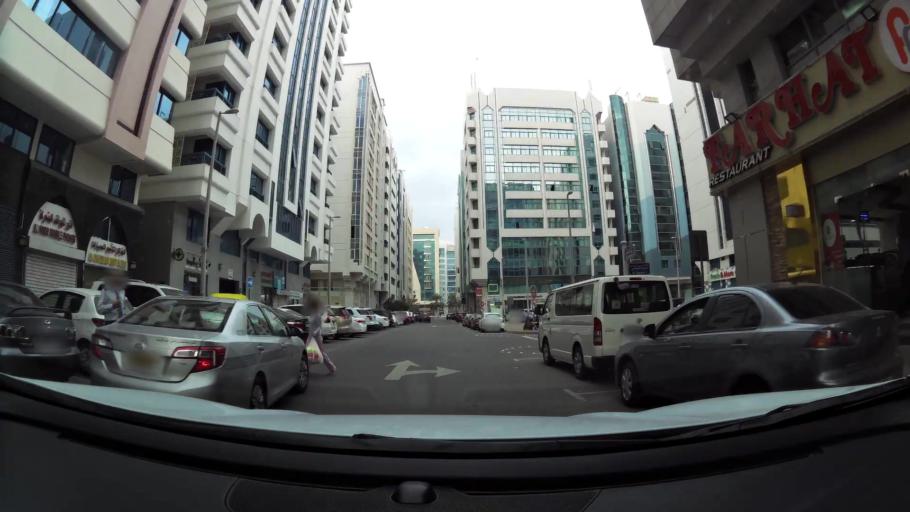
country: AE
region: Abu Dhabi
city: Abu Dhabi
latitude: 24.4901
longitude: 54.3835
